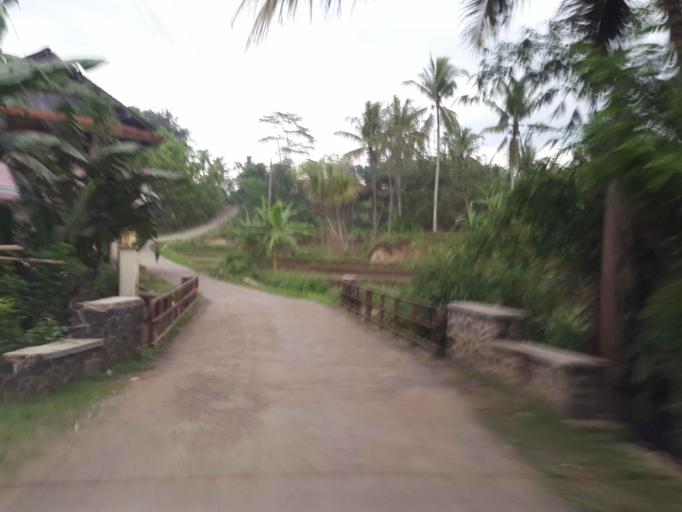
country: ID
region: Central Java
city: Bantarmangu
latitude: -7.3498
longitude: 108.8950
